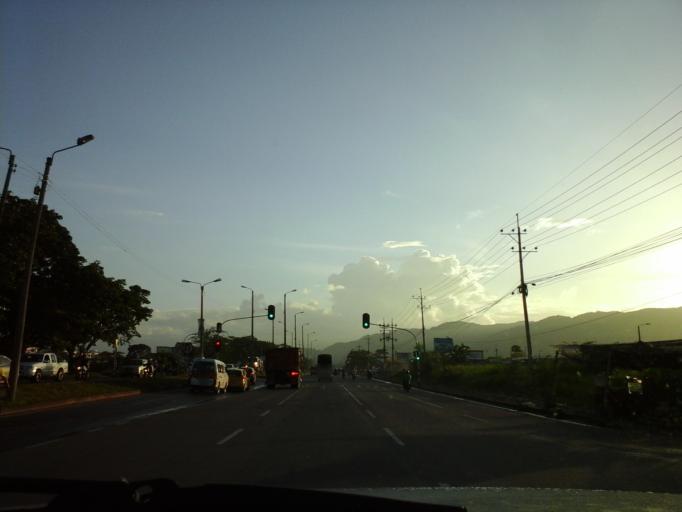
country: CO
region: Meta
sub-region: Villavicencio
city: Villavicencio
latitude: 4.1180
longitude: -73.6218
